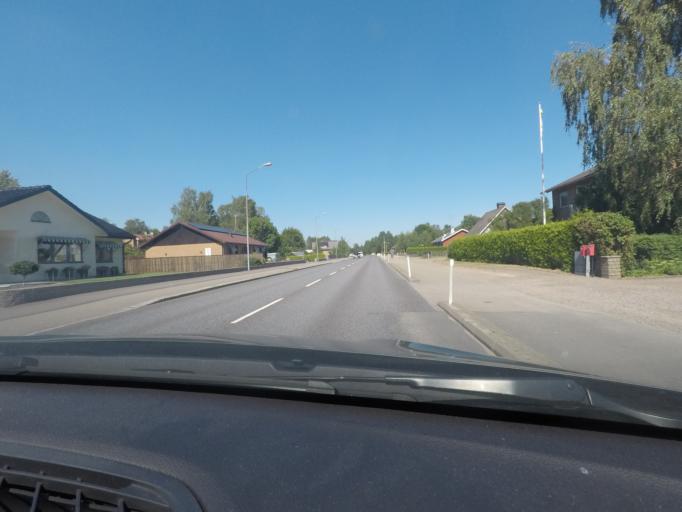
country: SE
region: Kronoberg
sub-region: Markaryds Kommun
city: Markaryd
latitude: 56.4692
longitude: 13.6018
